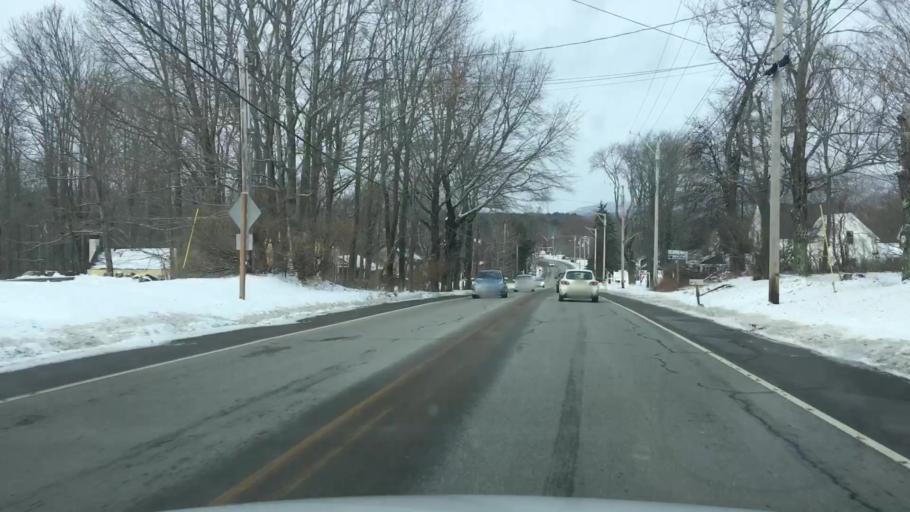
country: US
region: Maine
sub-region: Knox County
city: Rockport
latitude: 44.1760
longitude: -69.0798
